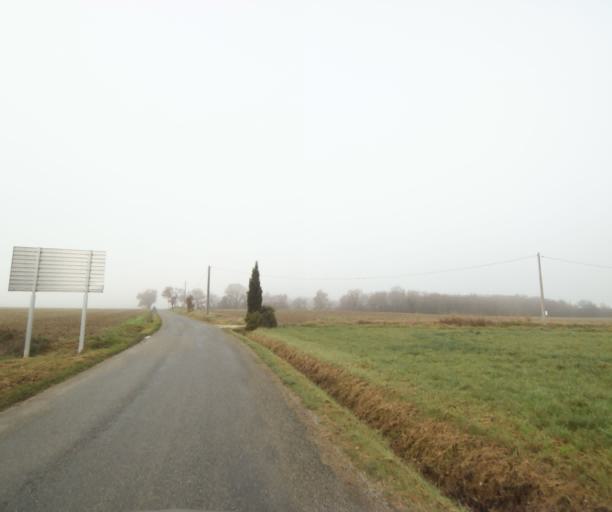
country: FR
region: Midi-Pyrenees
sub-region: Departement de la Haute-Garonne
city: Villaudric
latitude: 43.8295
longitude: 1.4734
